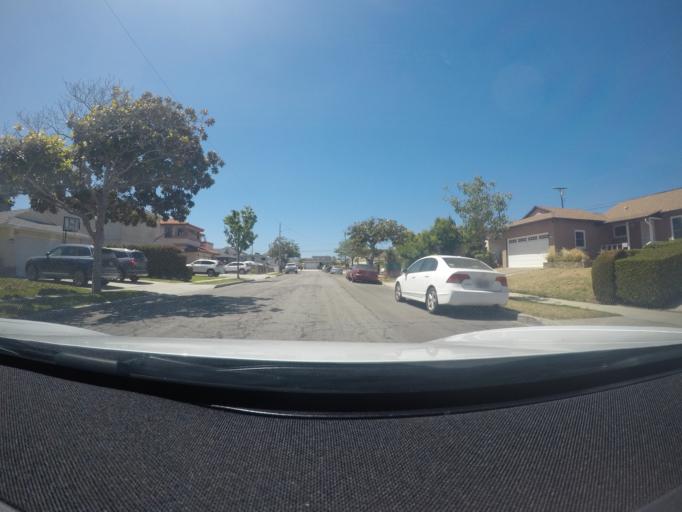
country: US
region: California
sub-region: Los Angeles County
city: Torrance
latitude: 33.8500
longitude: -118.3593
